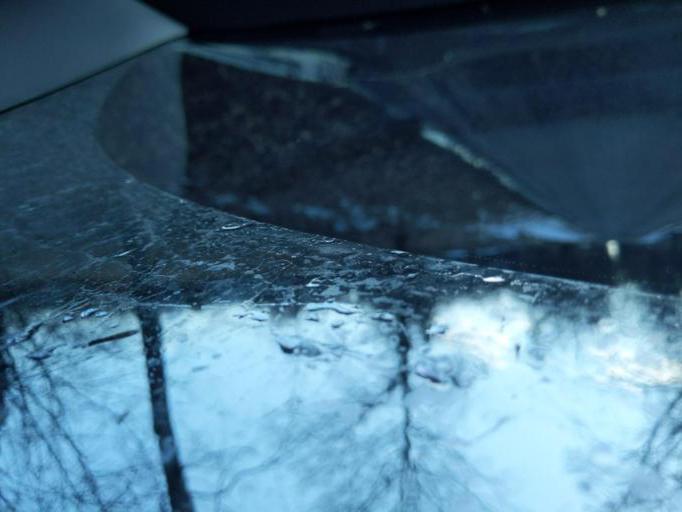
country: US
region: Michigan
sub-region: Ingham County
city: Stockbridge
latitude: 42.5179
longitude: -84.1679
